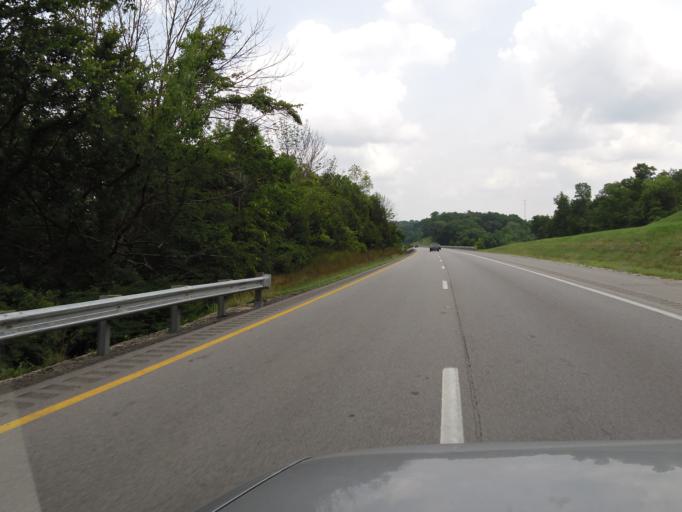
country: US
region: Indiana
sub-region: Switzerland County
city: Vevay
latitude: 38.6752
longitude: -84.9915
